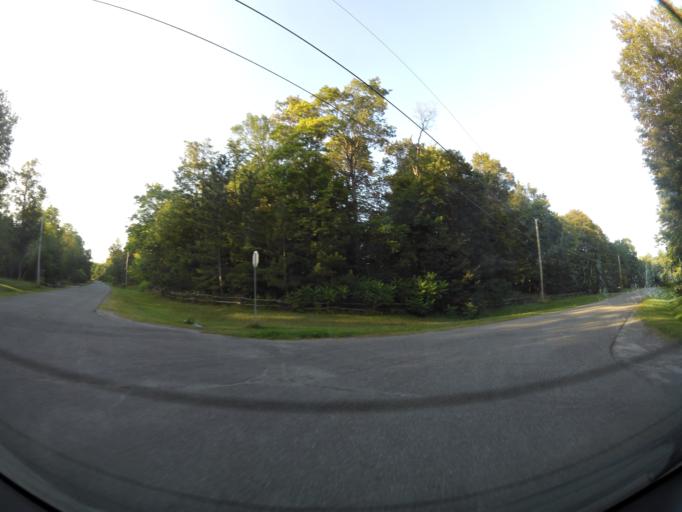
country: CA
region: Ontario
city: Clarence-Rockland
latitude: 45.5012
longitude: -75.4258
